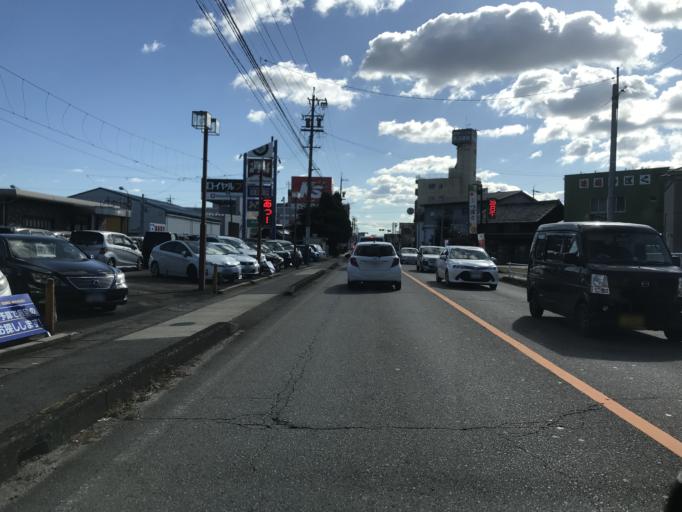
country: JP
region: Aichi
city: Nagoya-shi
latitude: 35.2084
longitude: 136.8551
